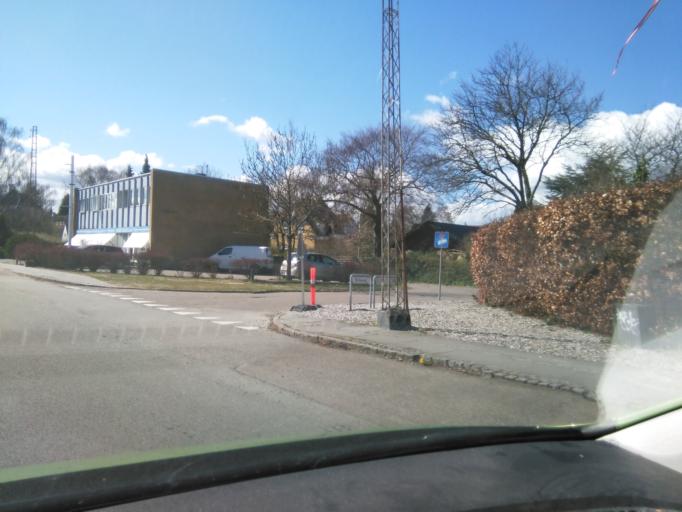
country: DK
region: Central Jutland
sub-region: Arhus Kommune
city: Arhus
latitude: 56.1914
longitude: 10.2403
